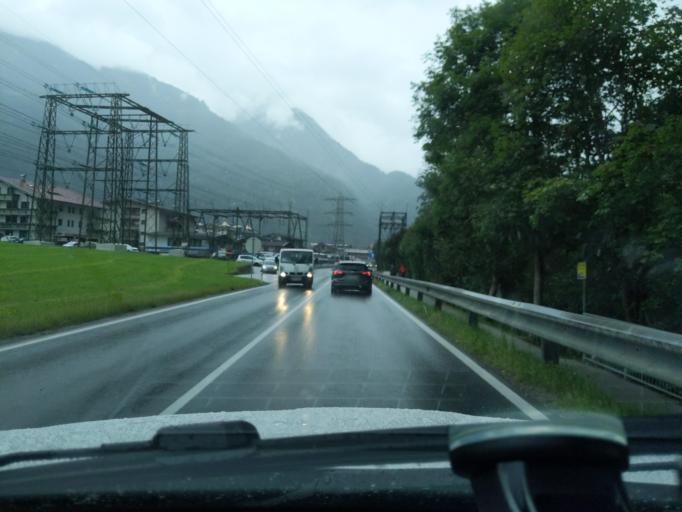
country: AT
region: Tyrol
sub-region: Politischer Bezirk Schwaz
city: Mayrhofen
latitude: 47.1662
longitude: 11.8566
